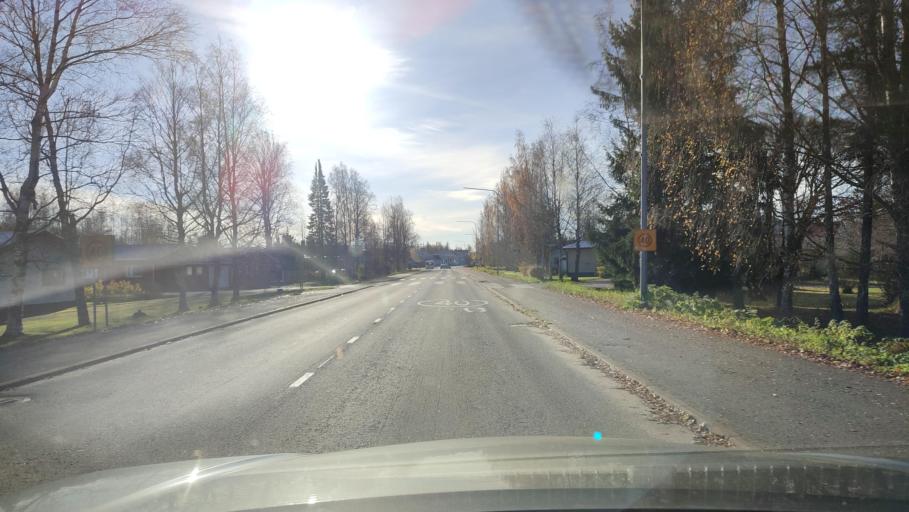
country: FI
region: Southern Ostrobothnia
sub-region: Suupohja
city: Teuva
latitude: 62.4893
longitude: 21.7466
